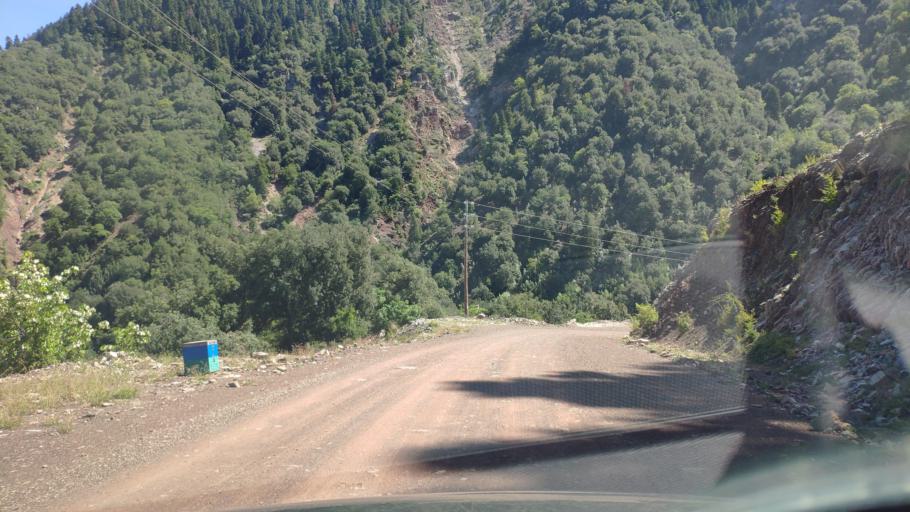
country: GR
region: Central Greece
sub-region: Nomos Evrytanias
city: Kerasochori
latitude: 39.1159
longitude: 21.6247
